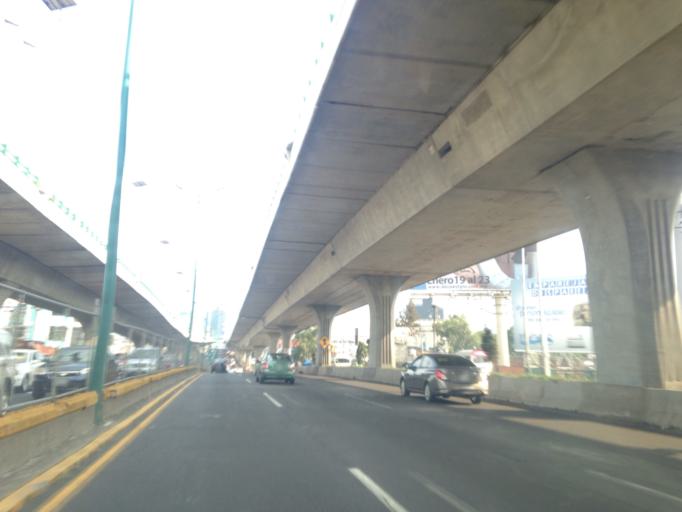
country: MX
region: Mexico
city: Naucalpan de Juarez
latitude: 19.4740
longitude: -99.2289
